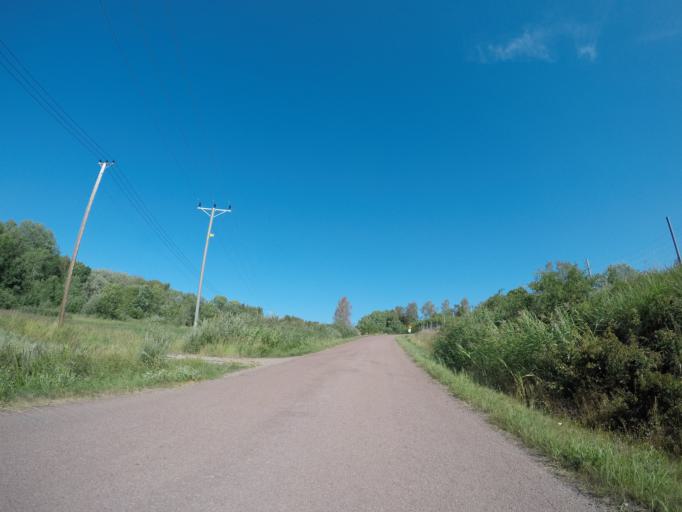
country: AX
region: Alands landsbygd
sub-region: Finstroem
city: Finstroem
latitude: 60.2716
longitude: 19.9233
